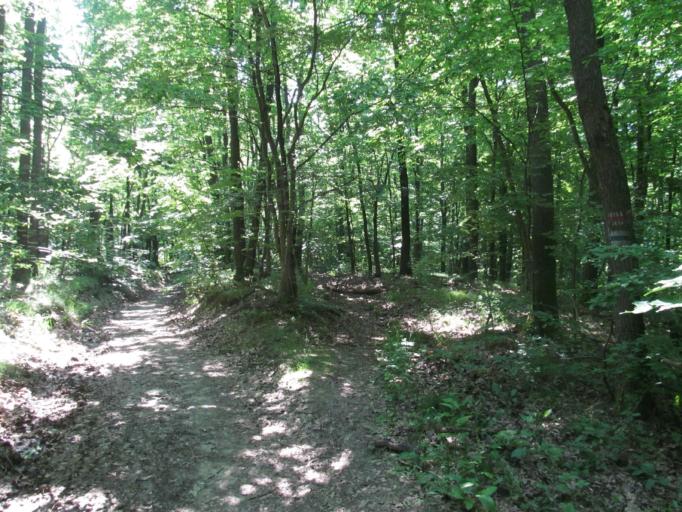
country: HU
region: Pest
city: Pilisszentkereszt
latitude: 47.7094
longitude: 18.9453
